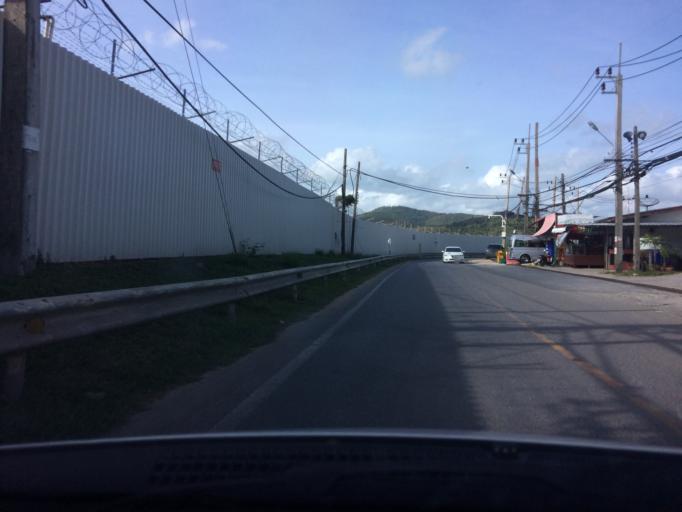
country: TH
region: Phuket
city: Thalang
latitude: 8.1102
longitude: 98.3095
